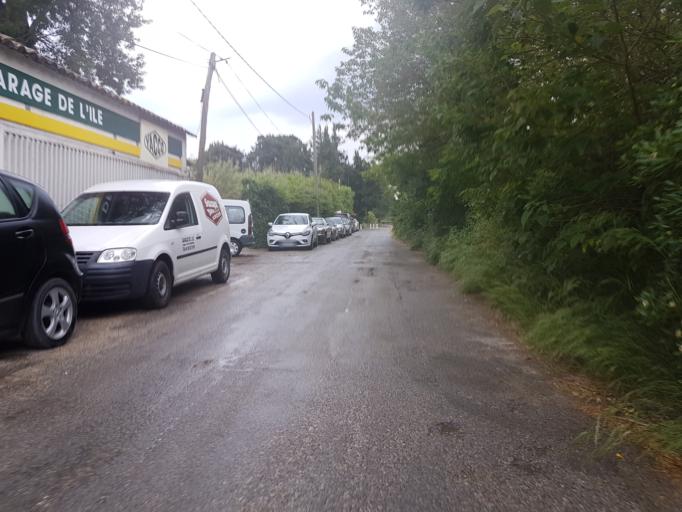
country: FR
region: Provence-Alpes-Cote d'Azur
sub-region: Departement du Vaucluse
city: Avignon
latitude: 43.9640
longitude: 4.8160
